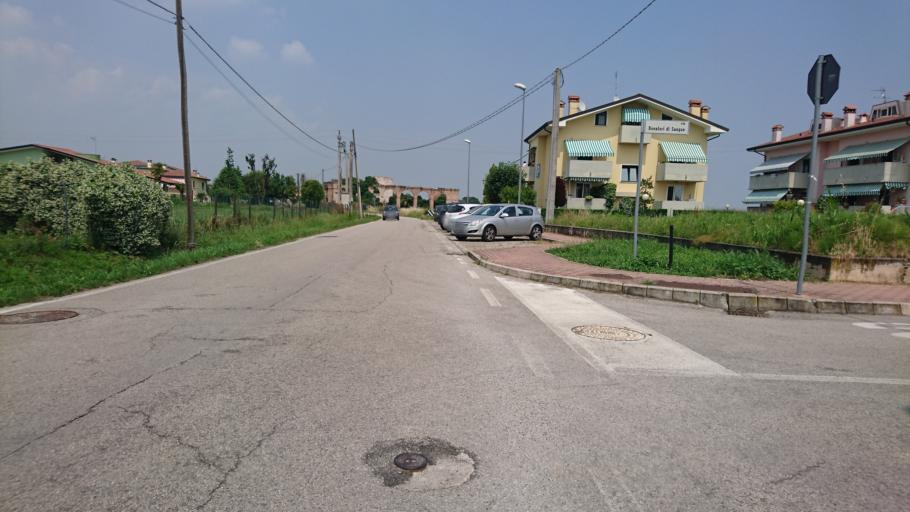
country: IT
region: Veneto
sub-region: Provincia di Padova
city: Cartura
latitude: 45.2707
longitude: 11.8573
